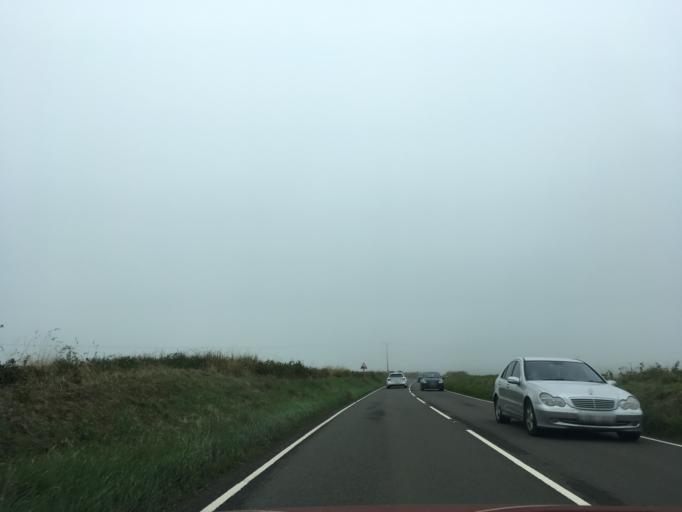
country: GB
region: Wales
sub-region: Pembrokeshire
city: Llanrhian
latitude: 51.8753
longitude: -5.1651
